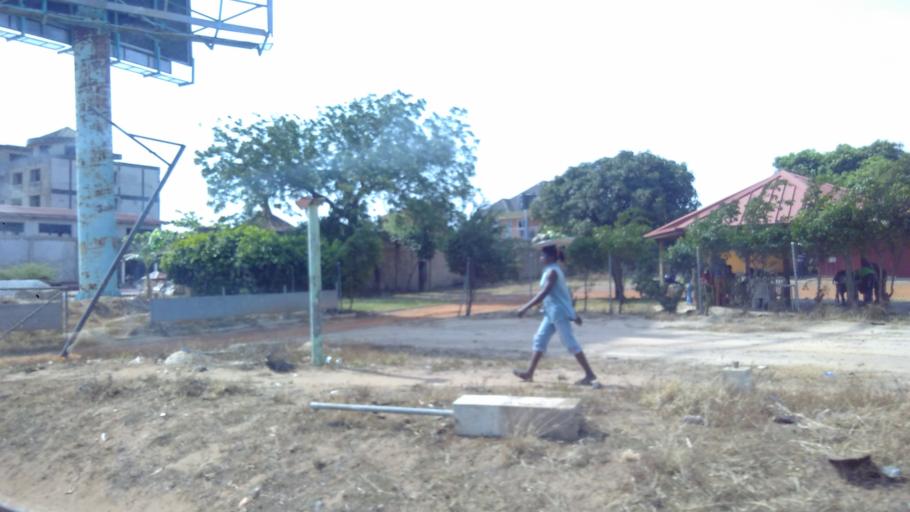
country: GH
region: Greater Accra
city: Nungua
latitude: 5.6144
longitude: -0.0711
